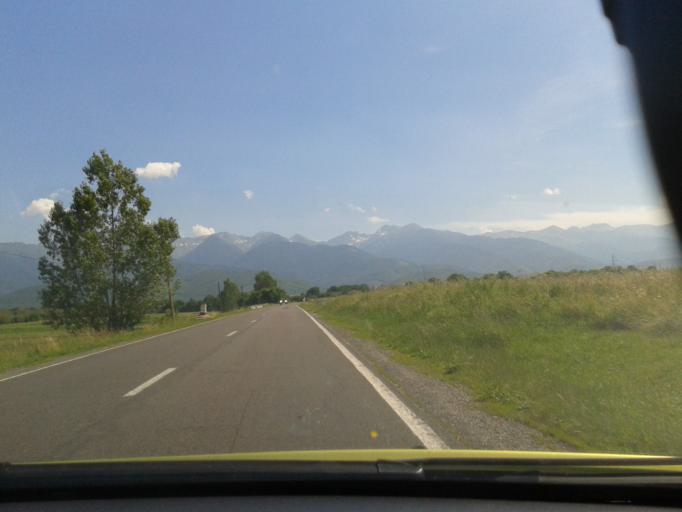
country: RO
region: Sibiu
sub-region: Comuna Cartisoara
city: Cartisoara
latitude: 45.7368
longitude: 24.5748
